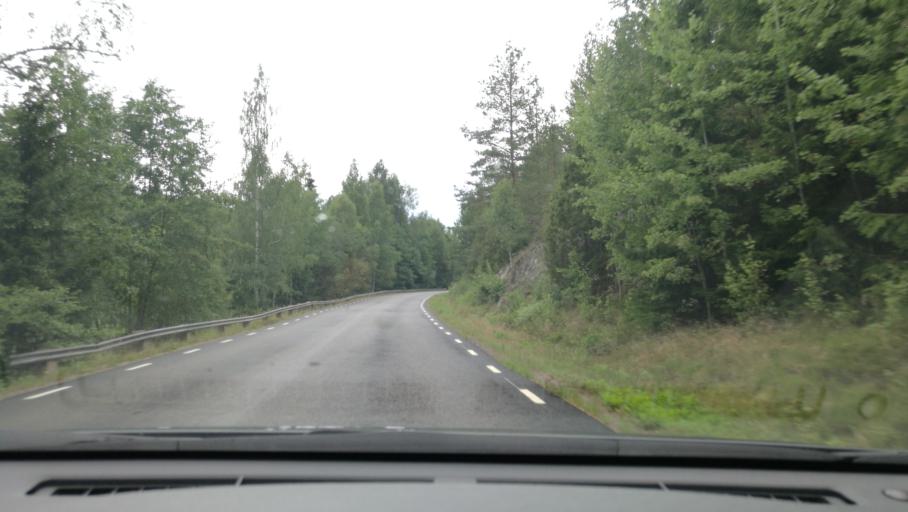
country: SE
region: OEstergoetland
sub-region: Norrkopings Kommun
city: Jursla
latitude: 58.8091
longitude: 16.0991
